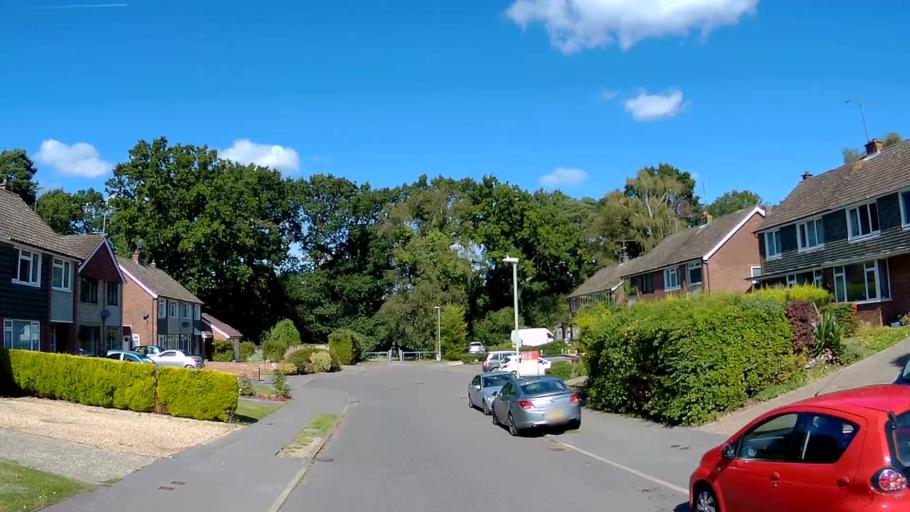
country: GB
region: England
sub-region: Bracknell Forest
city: Crowthorne
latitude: 51.3780
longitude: -0.8012
